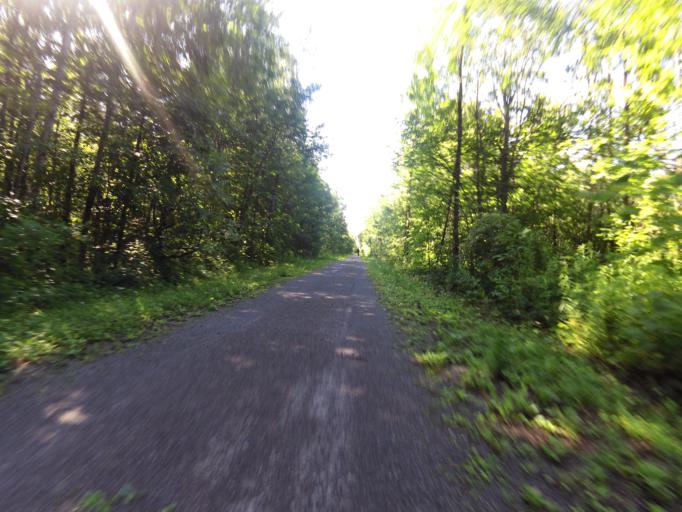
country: CA
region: Ontario
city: Ottawa
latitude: 45.1858
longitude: -75.6204
